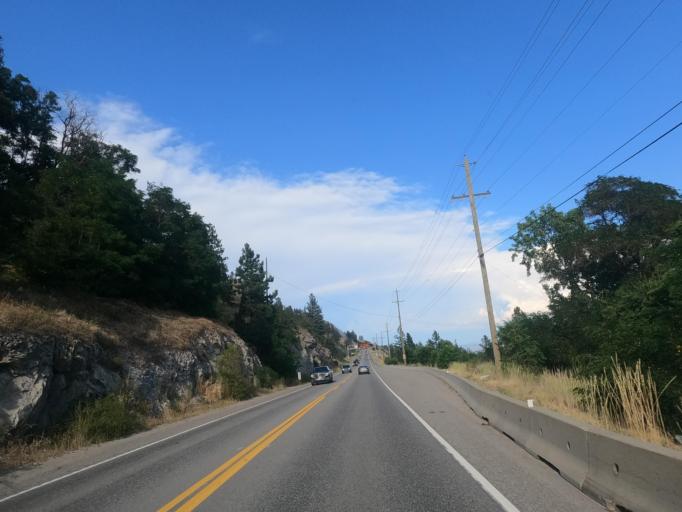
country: CA
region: British Columbia
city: Peachland
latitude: 49.7960
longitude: -119.6950
